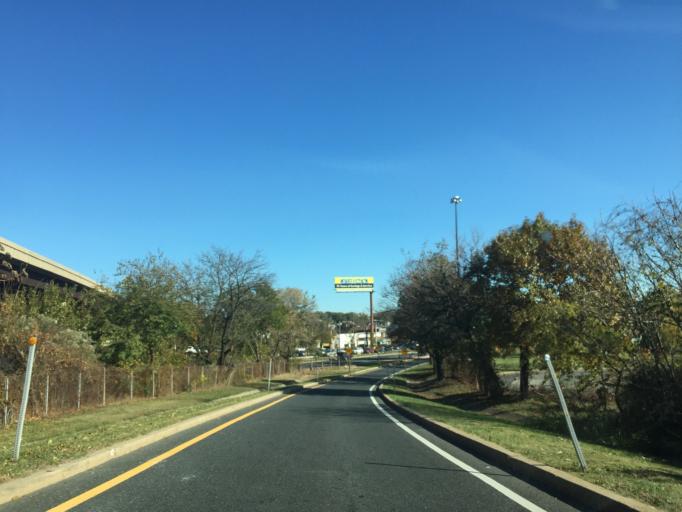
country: US
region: Maryland
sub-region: Baltimore County
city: Dundalk
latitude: 39.2840
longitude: -76.5390
